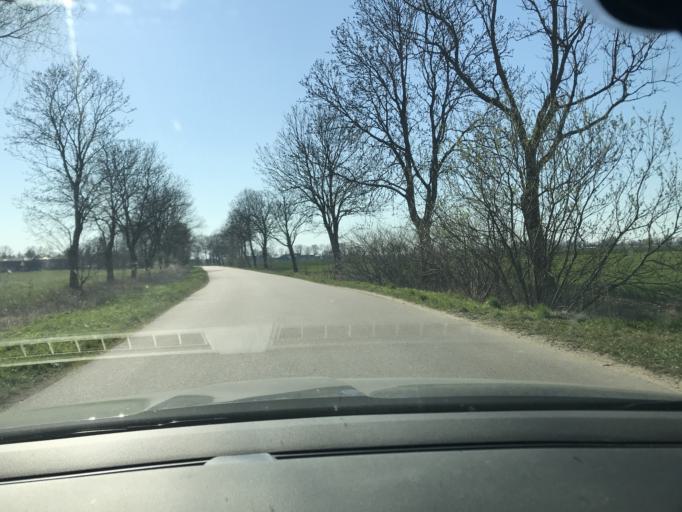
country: PL
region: Pomeranian Voivodeship
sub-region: Powiat nowodworski
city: Stegna
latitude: 54.2935
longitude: 19.1232
